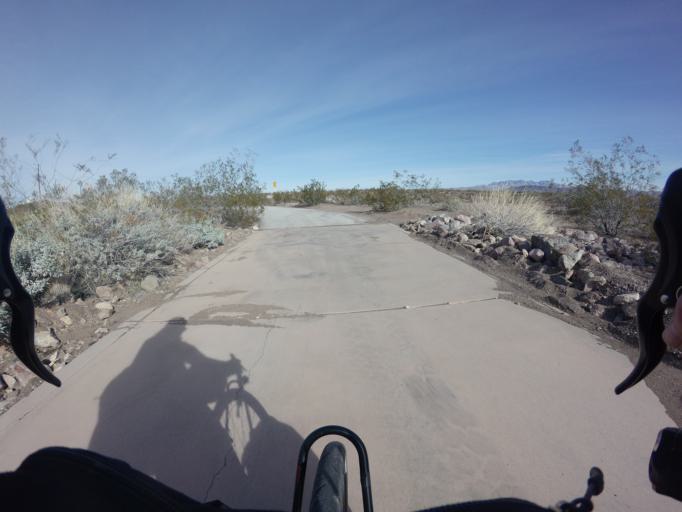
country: US
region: Nevada
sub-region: Clark County
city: Boulder City
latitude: 36.0723
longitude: -114.8113
